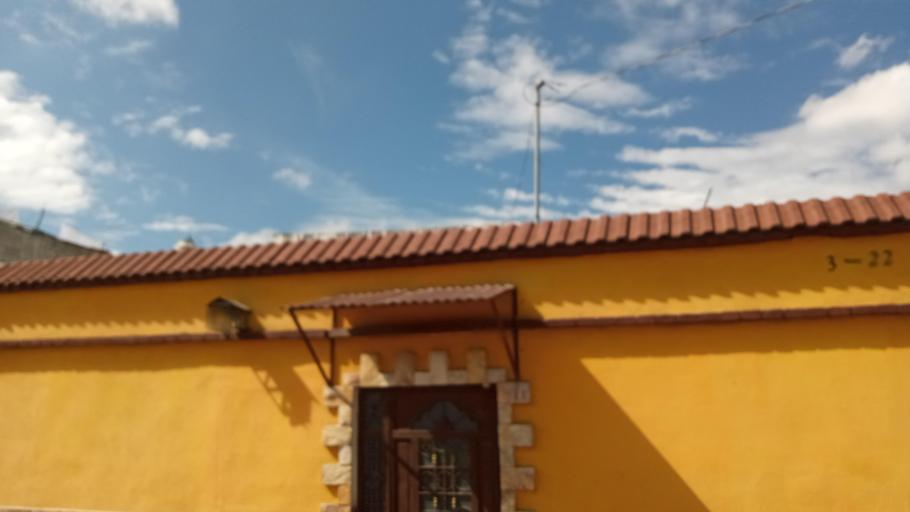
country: GT
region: Quetzaltenango
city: Quetzaltenango
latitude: 14.8439
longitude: -91.5061
